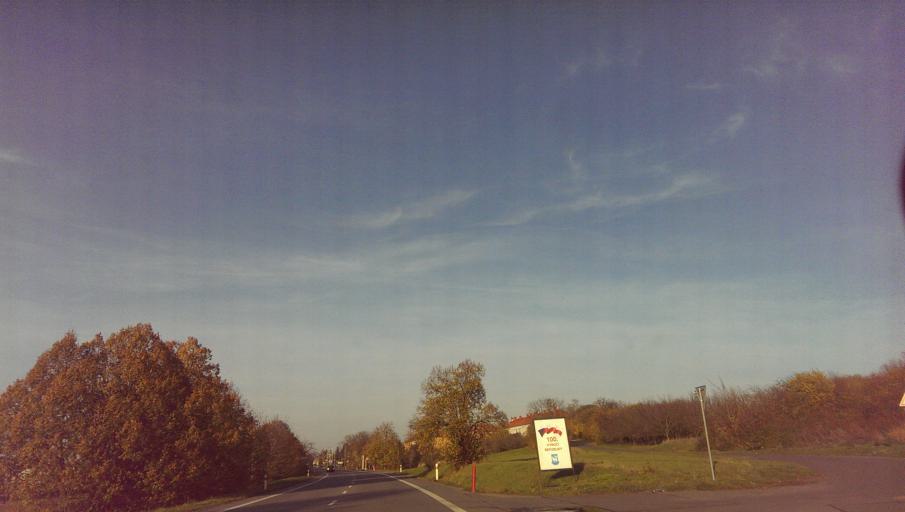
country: CZ
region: Zlin
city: Kunovice
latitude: 49.0296
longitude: 17.4586
